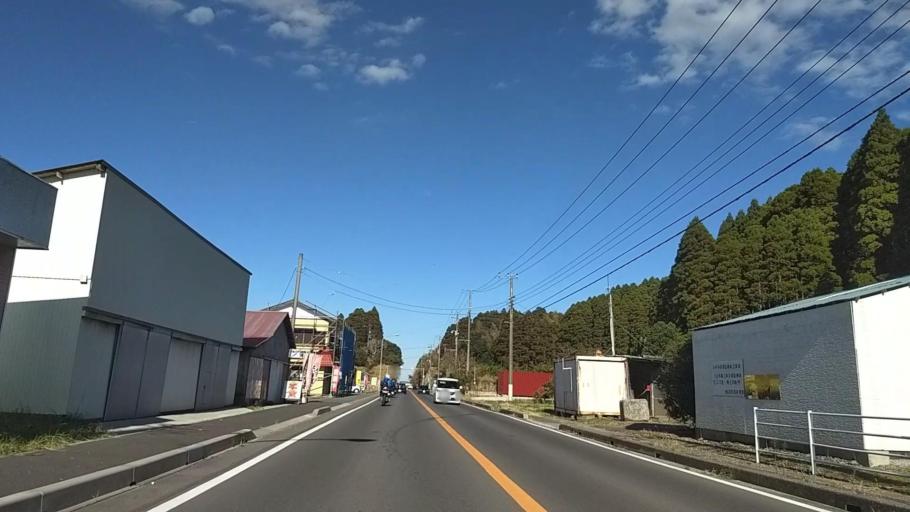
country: JP
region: Chiba
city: Ohara
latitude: 35.2134
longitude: 140.3764
